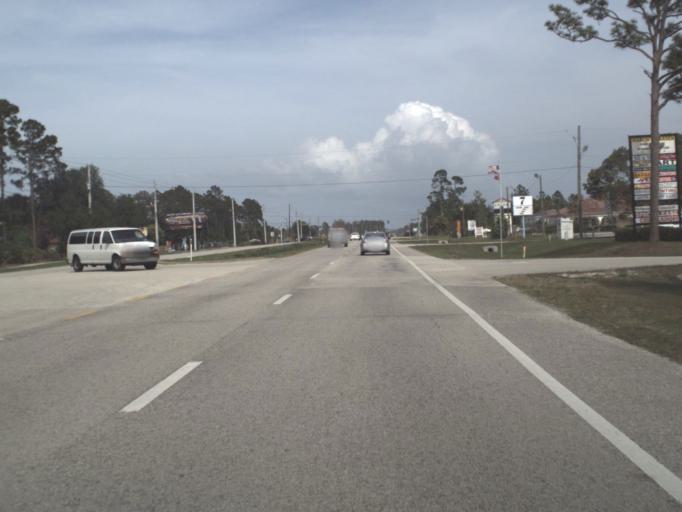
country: US
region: Florida
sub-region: Flagler County
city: Bunnell
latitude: 29.4756
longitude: -81.2261
